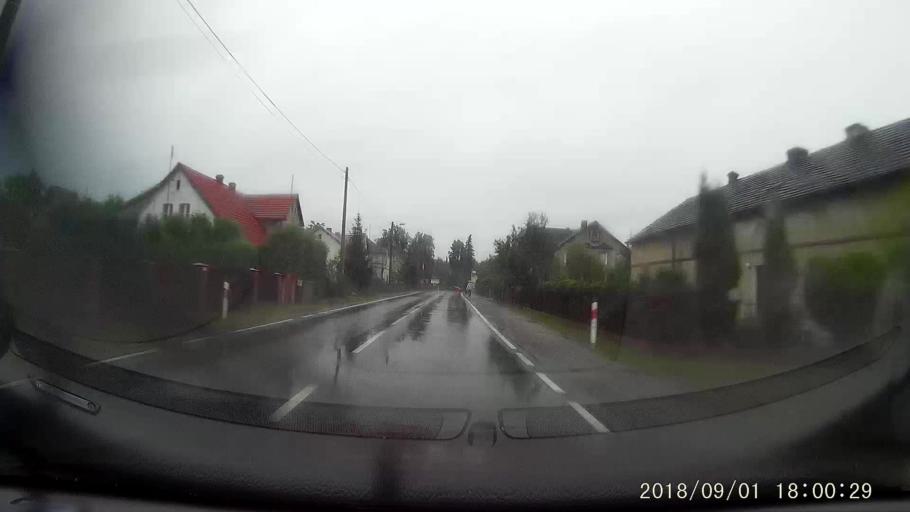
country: PL
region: Lubusz
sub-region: Powiat zaganski
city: Gozdnica
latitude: 51.4019
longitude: 15.1830
